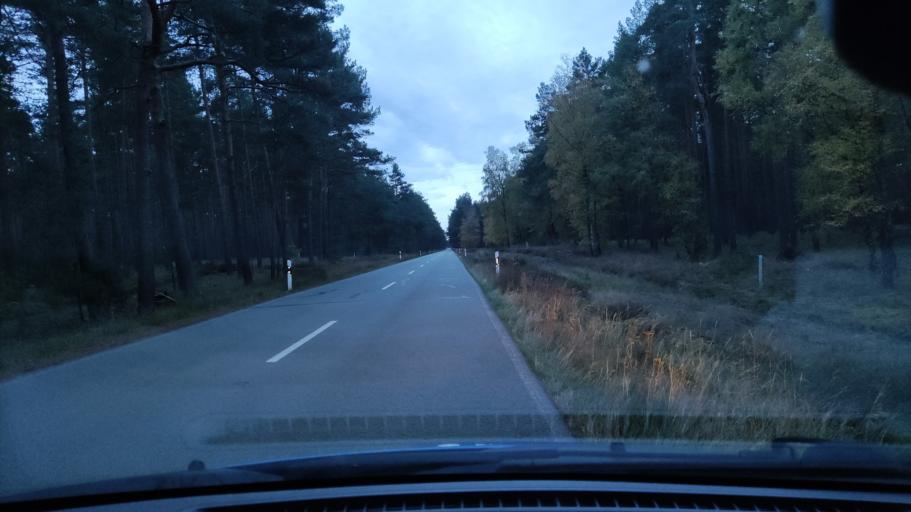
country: DE
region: Lower Saxony
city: Prezelle
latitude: 53.0073
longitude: 11.3905
